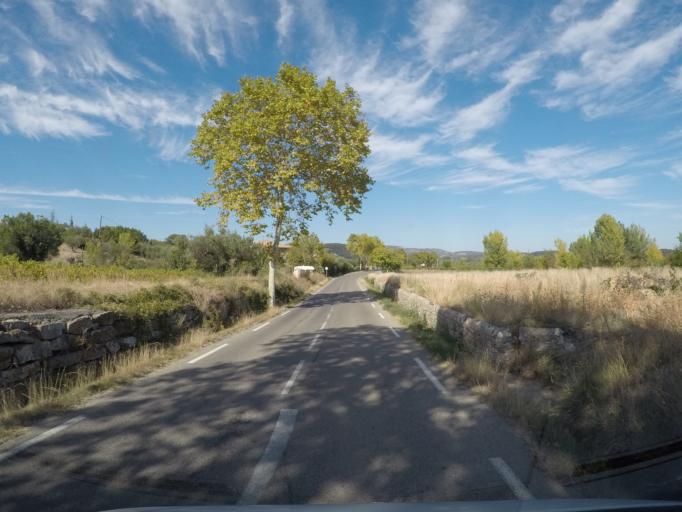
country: FR
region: Languedoc-Roussillon
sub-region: Departement du Gard
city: Boisset-et-Gaujac
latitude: 44.0267
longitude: 3.9980
